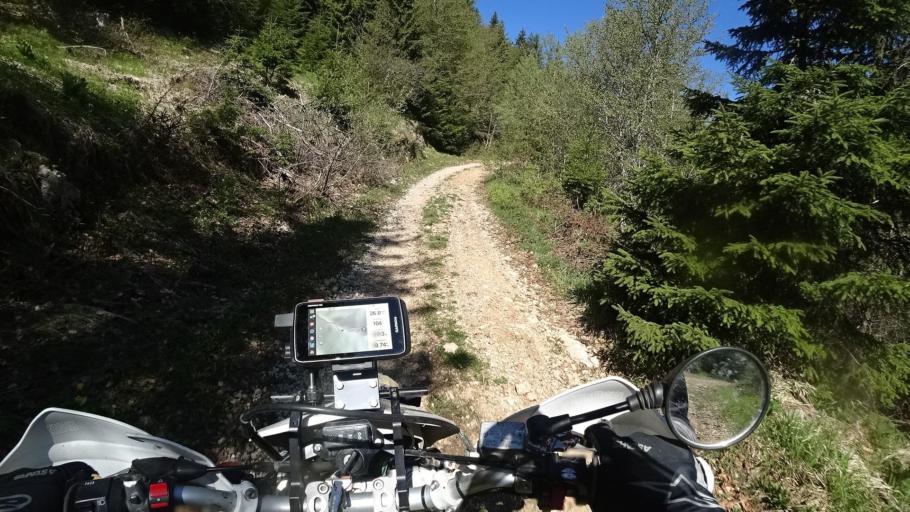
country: BA
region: Federation of Bosnia and Herzegovina
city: Rumboci
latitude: 43.8545
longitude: 17.5003
